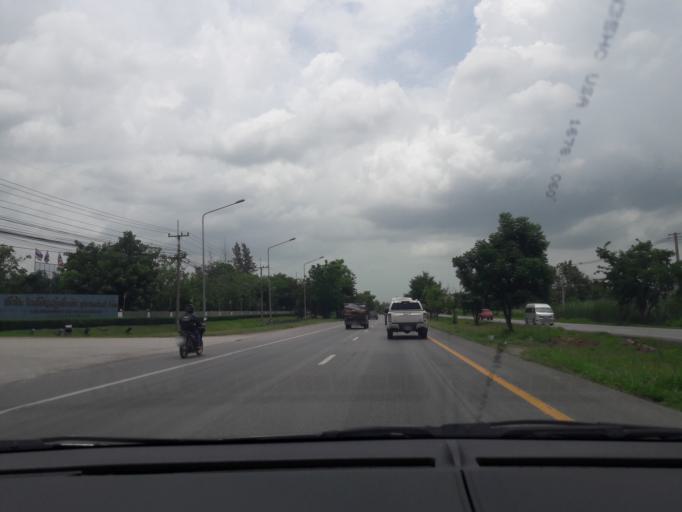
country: TH
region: Nakhon Ratchasima
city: Chaloem Phra Kiat
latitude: 15.0687
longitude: 102.2018
